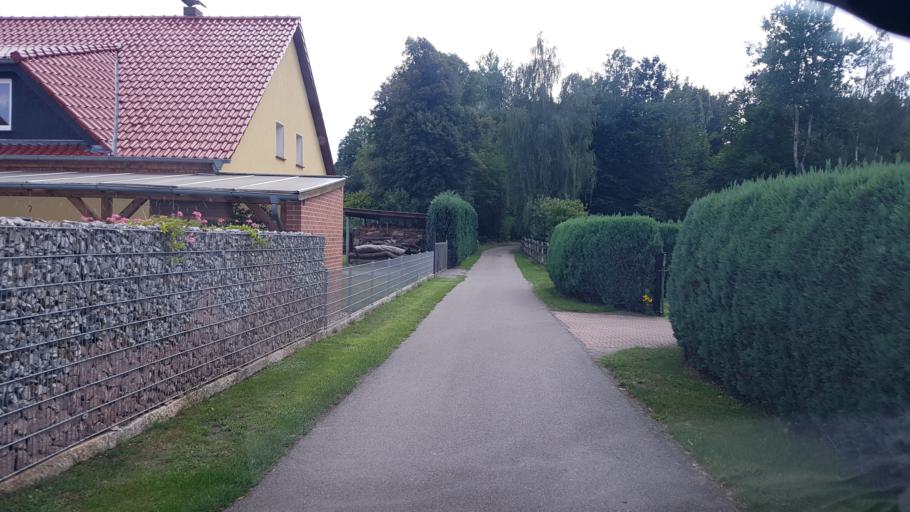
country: DE
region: Brandenburg
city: Calau
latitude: 51.7185
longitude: 13.9426
